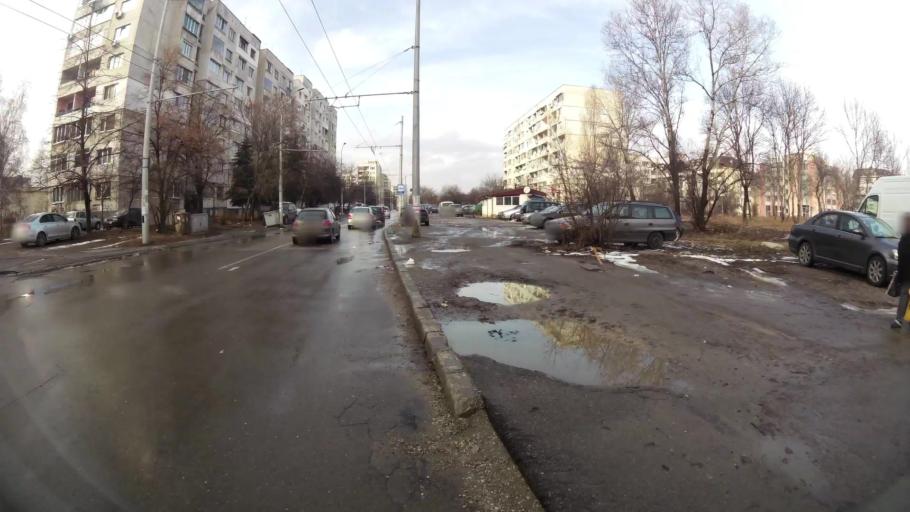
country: BG
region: Sofia-Capital
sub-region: Stolichna Obshtina
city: Sofia
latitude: 42.7163
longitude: 23.2763
